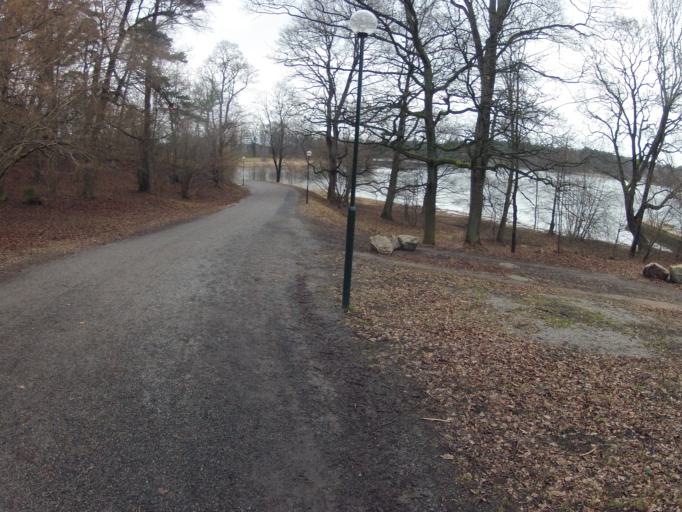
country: SE
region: Stockholm
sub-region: Norrtalje Kommun
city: Bergshamra
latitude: 59.3594
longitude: 18.0395
